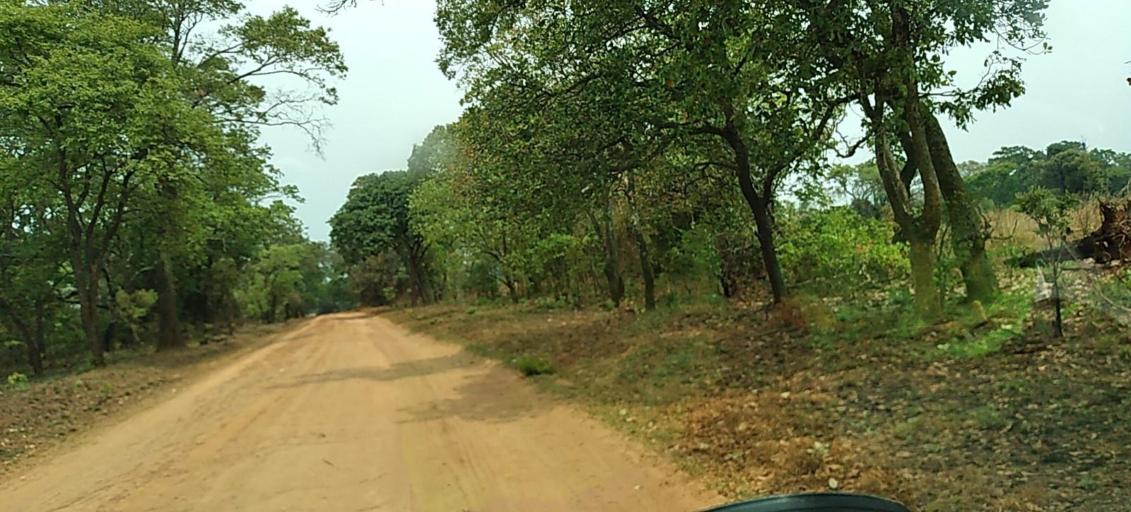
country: ZM
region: North-Western
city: Solwezi
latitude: -12.8175
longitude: 26.5360
